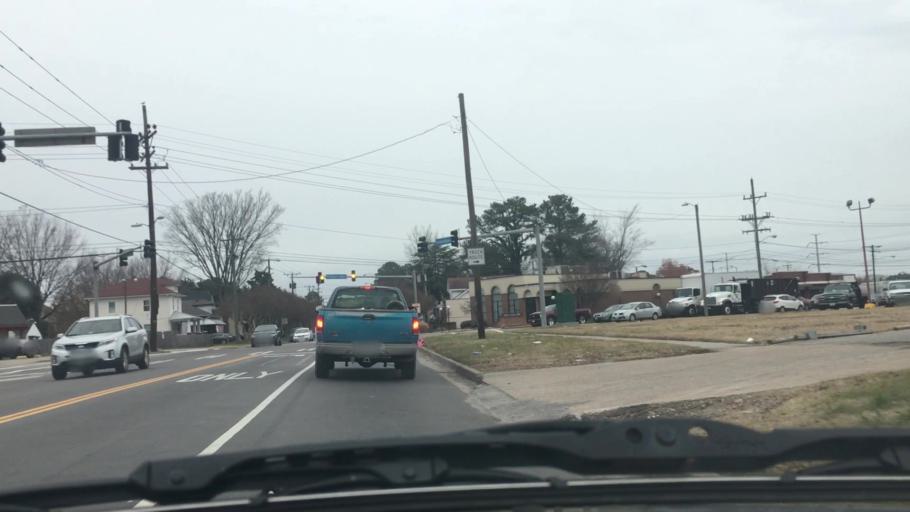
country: US
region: Virginia
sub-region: City of Norfolk
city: Norfolk
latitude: 36.8596
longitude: -76.2495
